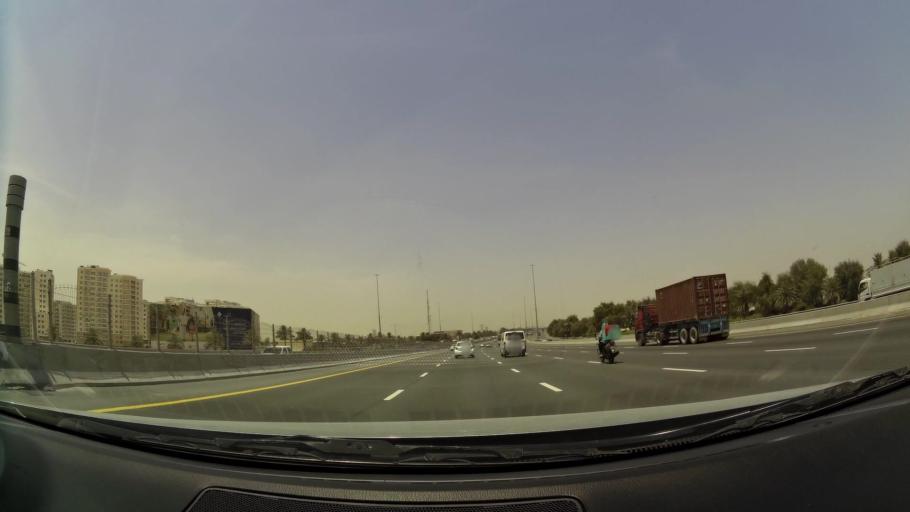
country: AE
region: Dubai
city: Dubai
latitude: 25.1188
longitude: 55.3629
